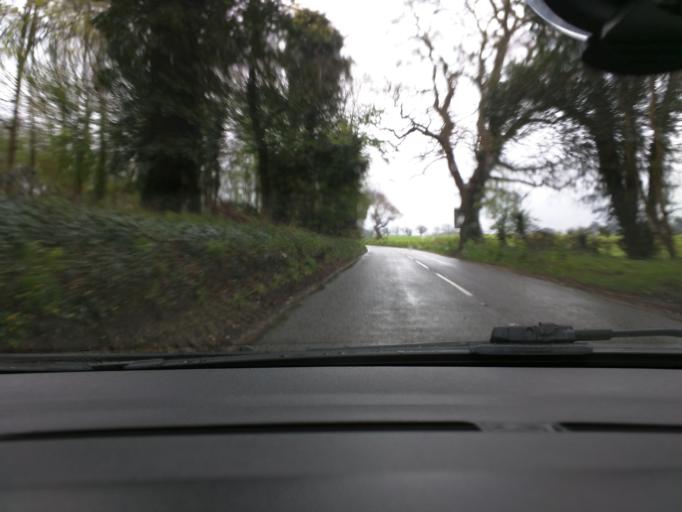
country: GB
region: England
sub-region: Suffolk
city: Leiston
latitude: 52.1791
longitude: 1.5386
